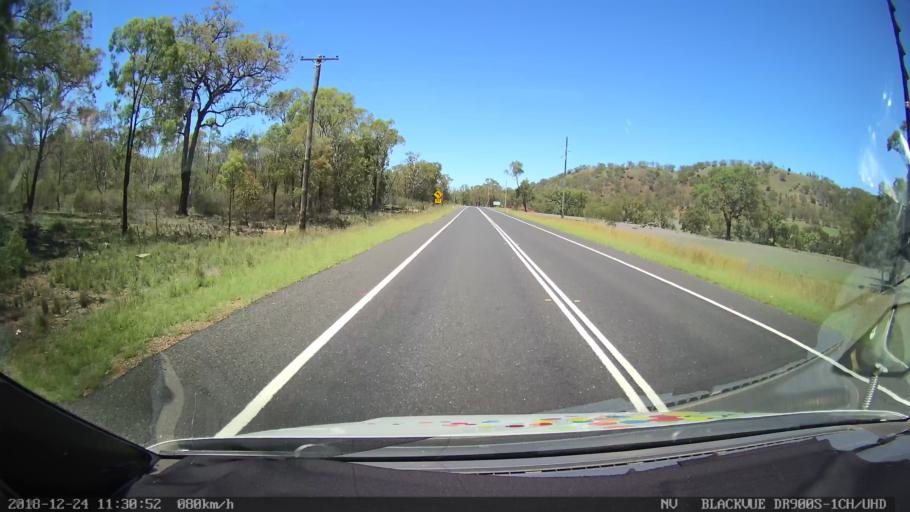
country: AU
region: New South Wales
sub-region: Upper Hunter Shire
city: Merriwa
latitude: -32.2092
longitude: 150.4630
